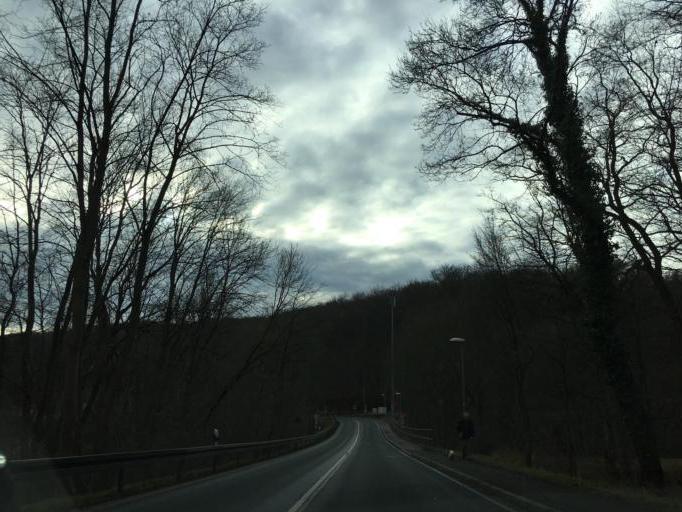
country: DE
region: Thuringia
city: Hetschburg
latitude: 50.9281
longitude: 11.2898
